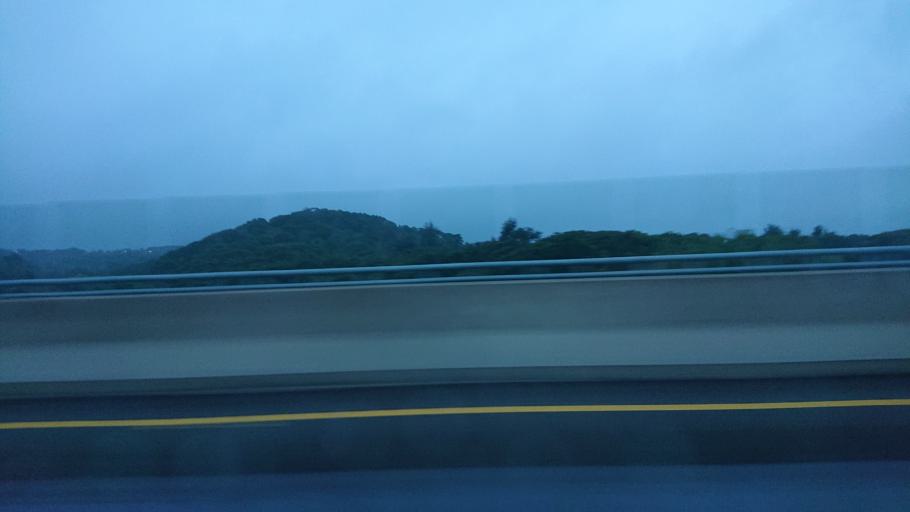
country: TW
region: Taiwan
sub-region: Miaoli
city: Miaoli
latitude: 24.5578
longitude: 120.7126
